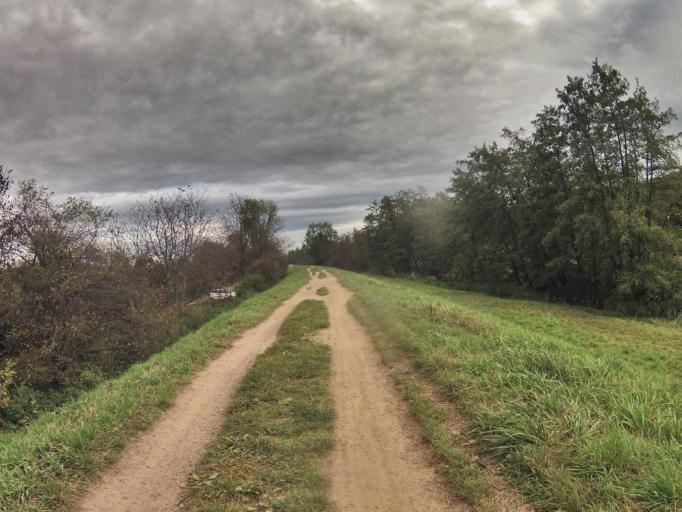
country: PL
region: Lesser Poland Voivodeship
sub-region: Krakow
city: Krakow
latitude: 50.0625
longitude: 19.8955
